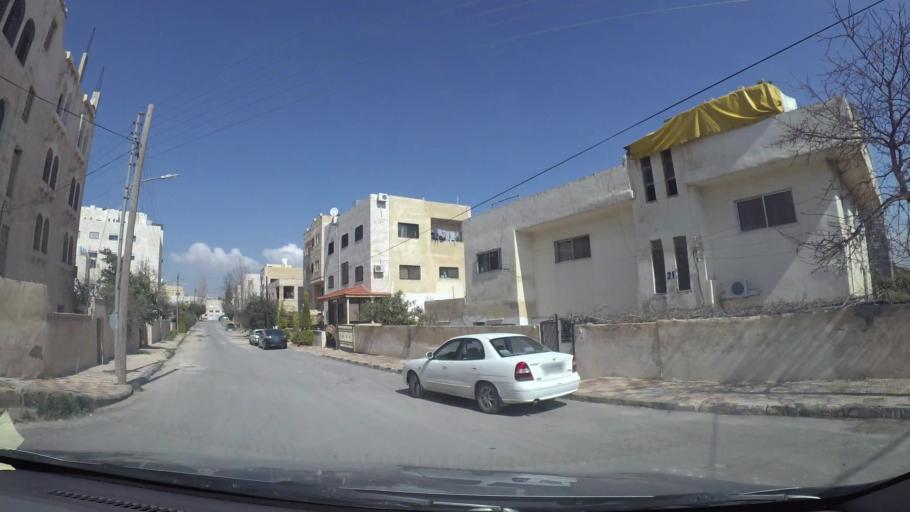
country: JO
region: Amman
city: Al Bunayyat ash Shamaliyah
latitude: 31.9026
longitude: 35.8999
